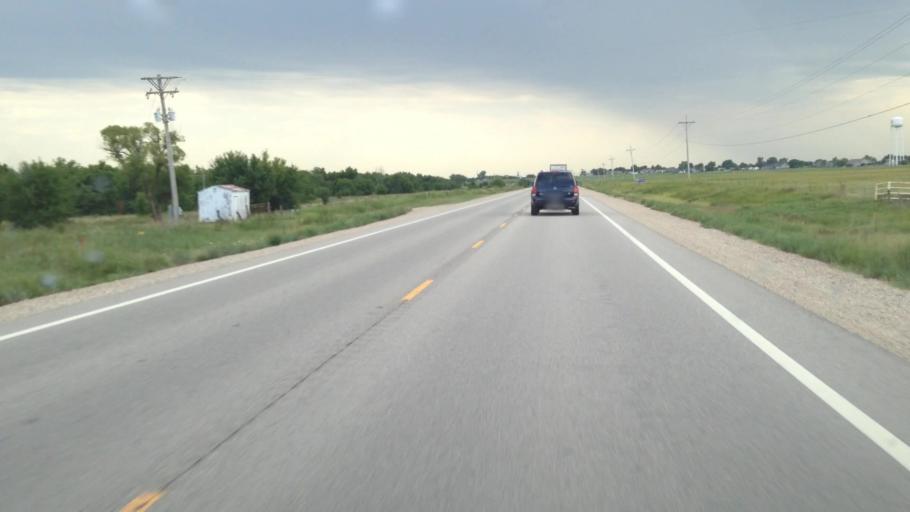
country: US
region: Kansas
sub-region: Coffey County
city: Burlington
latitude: 38.2821
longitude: -95.7382
